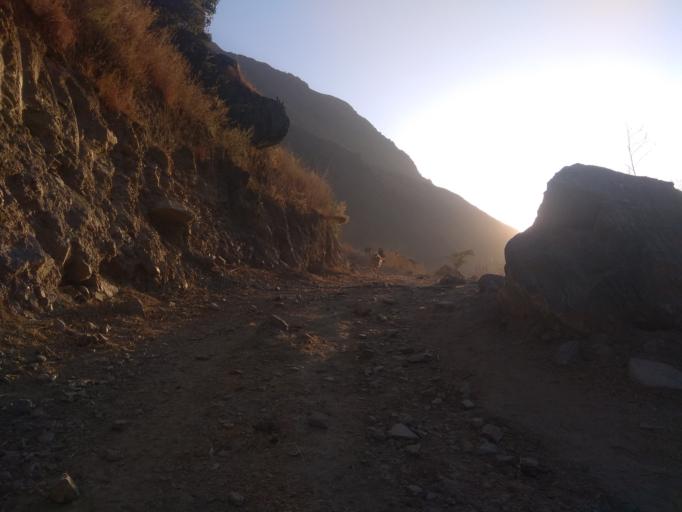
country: NP
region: Mid Western
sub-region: Bheri Zone
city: Dailekh
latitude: 29.2785
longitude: 81.7326
